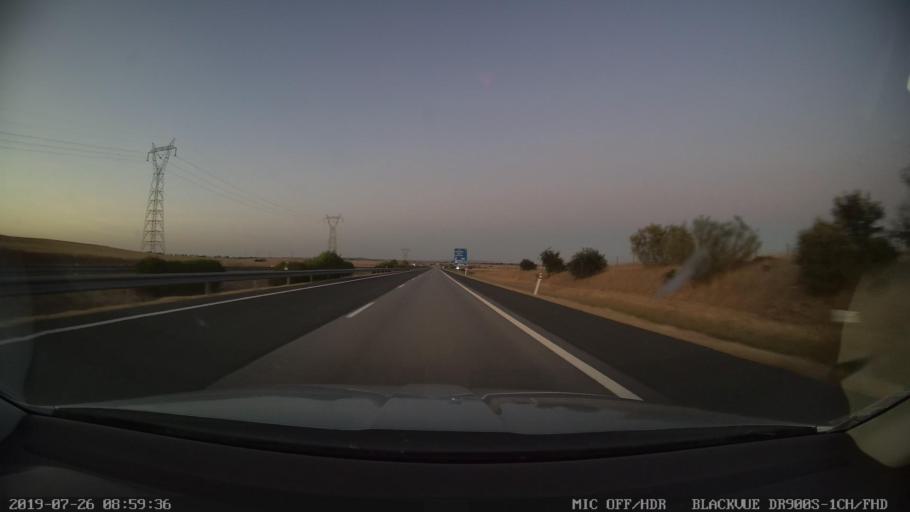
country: PT
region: Evora
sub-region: Evora
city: Evora
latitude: 38.6408
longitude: -7.8702
